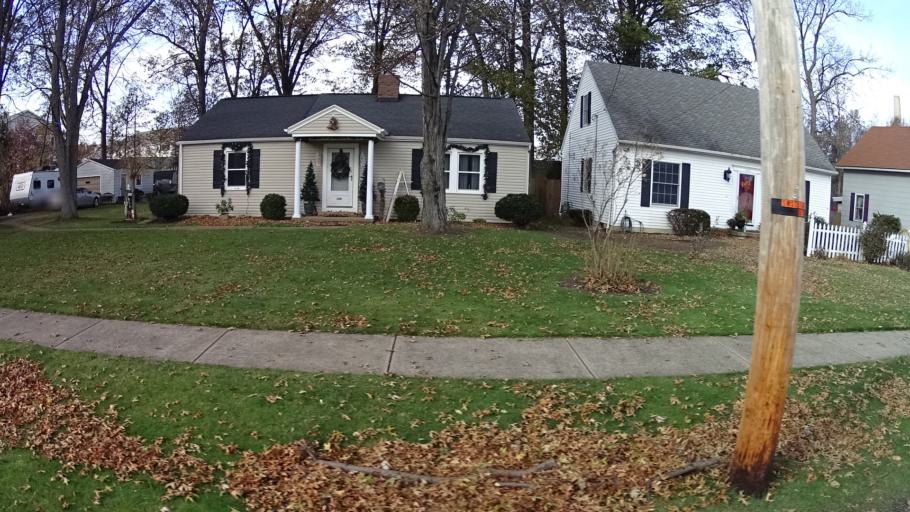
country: US
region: Ohio
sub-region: Lorain County
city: Avon Lake
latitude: 41.5007
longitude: -82.0481
